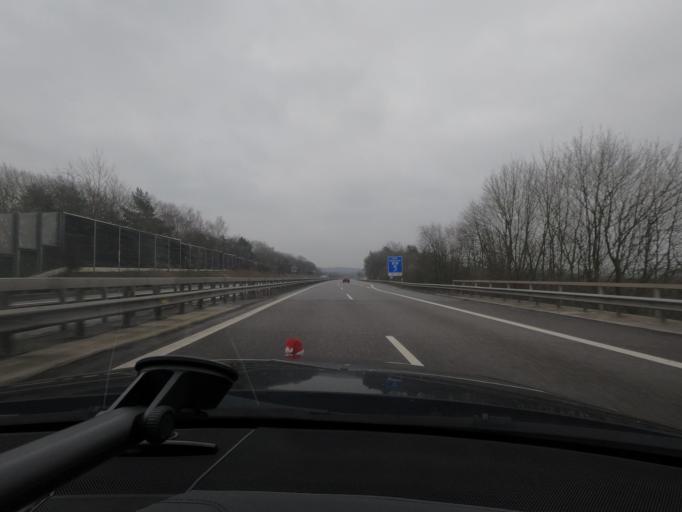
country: DE
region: Lower Saxony
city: Seevetal
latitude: 53.4267
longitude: 9.9579
